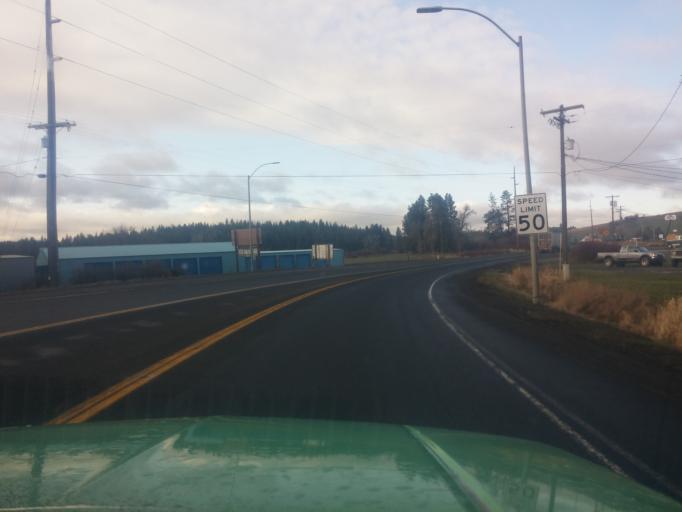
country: US
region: Idaho
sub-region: Latah County
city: Moscow
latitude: 46.9289
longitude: -116.9329
